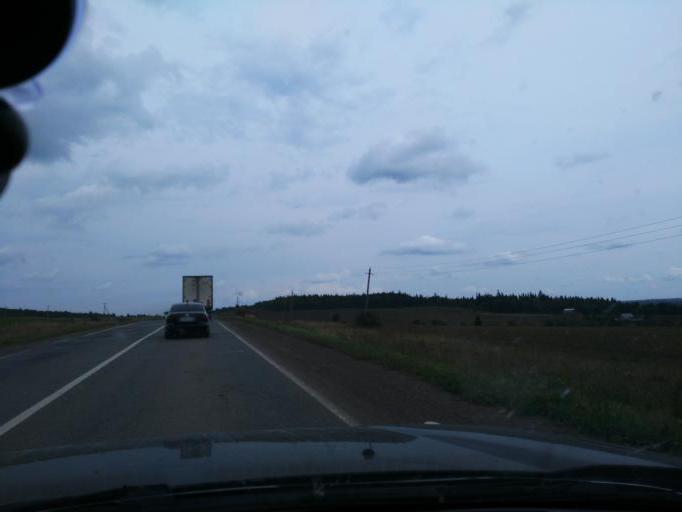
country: RU
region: Perm
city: Kuyeda
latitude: 56.4634
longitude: 55.6615
